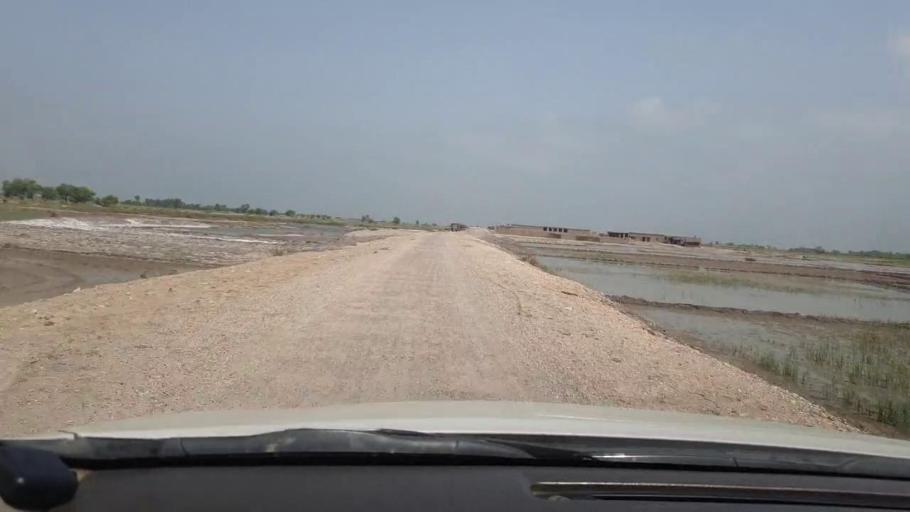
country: PK
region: Sindh
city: Shikarpur
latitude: 28.0008
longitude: 68.5589
